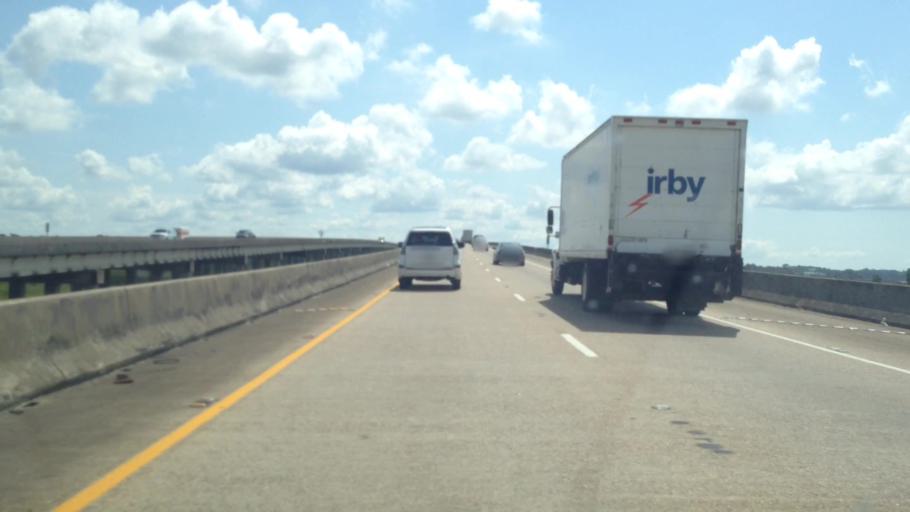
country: US
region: Mississippi
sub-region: Jackson County
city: Escatawpa
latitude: 30.4379
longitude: -88.5643
